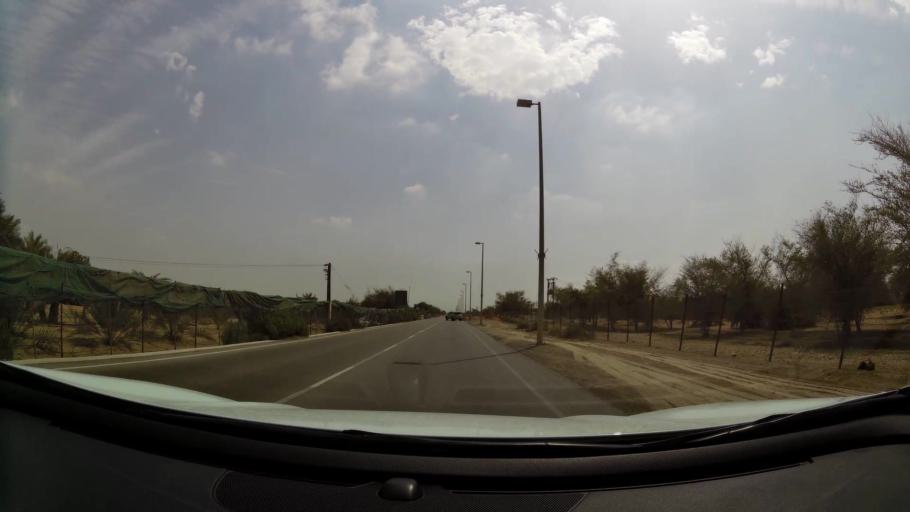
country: AE
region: Abu Dhabi
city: Abu Dhabi
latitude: 24.5205
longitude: 54.6516
